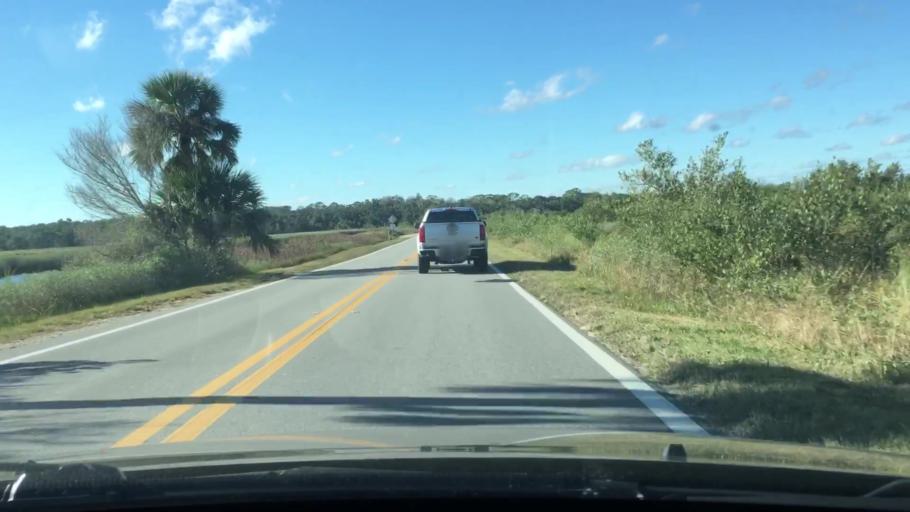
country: US
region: Florida
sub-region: Volusia County
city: Ormond-by-the-Sea
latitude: 29.3427
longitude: -81.0884
